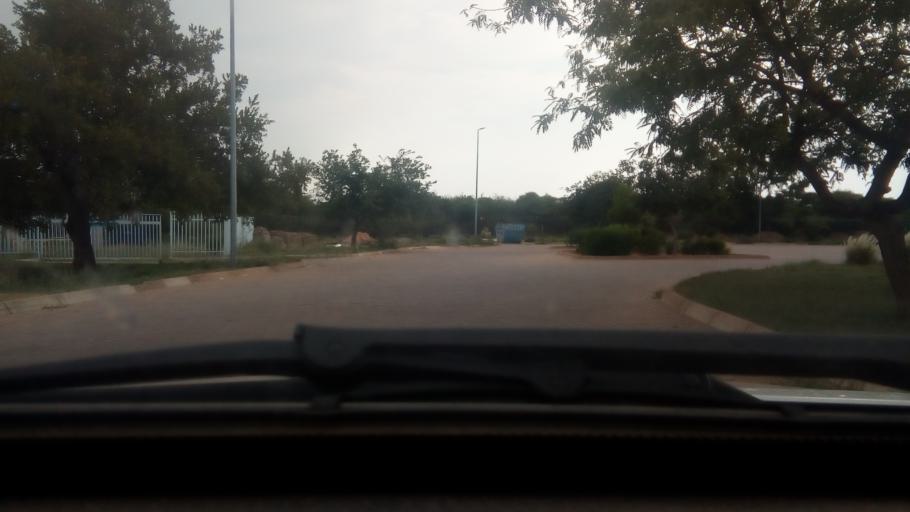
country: BW
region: South East
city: Gaborone
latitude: -24.7040
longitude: 26.0916
